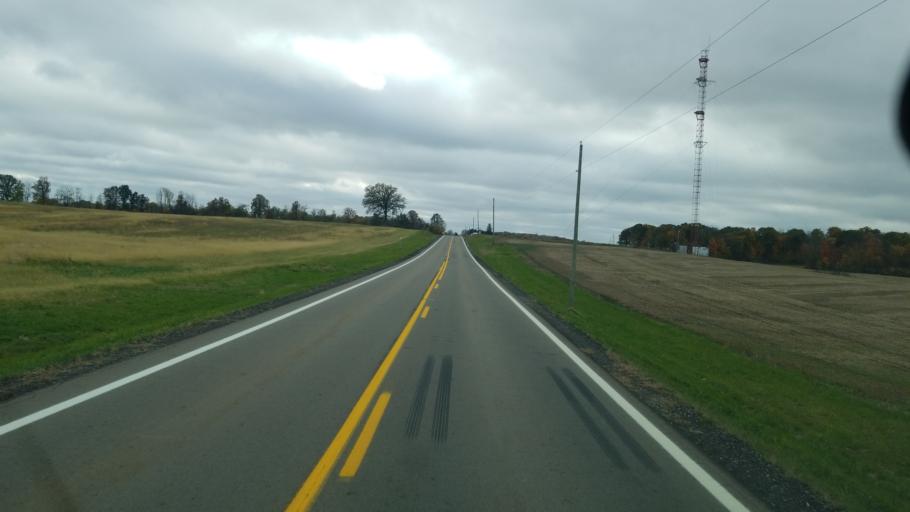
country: US
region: Ohio
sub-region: Richland County
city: Shelby
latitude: 40.8978
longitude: -82.7450
